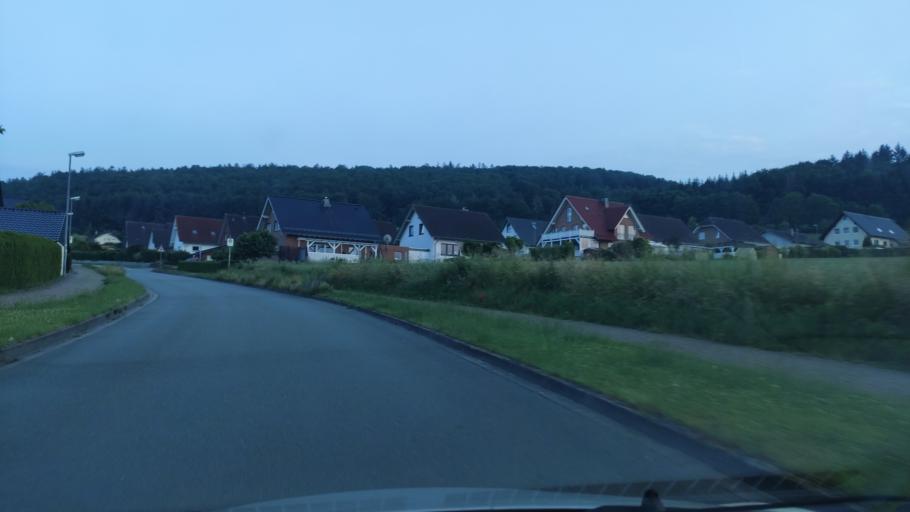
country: DE
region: North Rhine-Westphalia
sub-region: Regierungsbezirk Detmold
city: Hoexter
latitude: 51.7731
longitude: 9.3506
